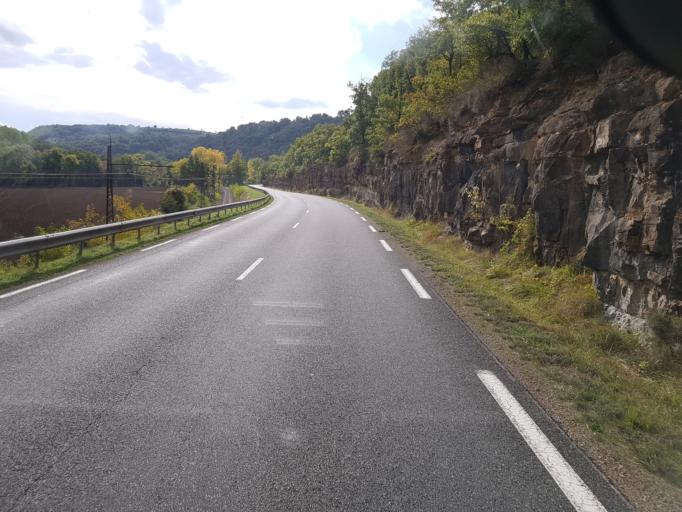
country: FR
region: Midi-Pyrenees
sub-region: Departement de l'Aveyron
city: Saint-Georges-de-Luzencon
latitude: 44.0400
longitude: 2.9663
